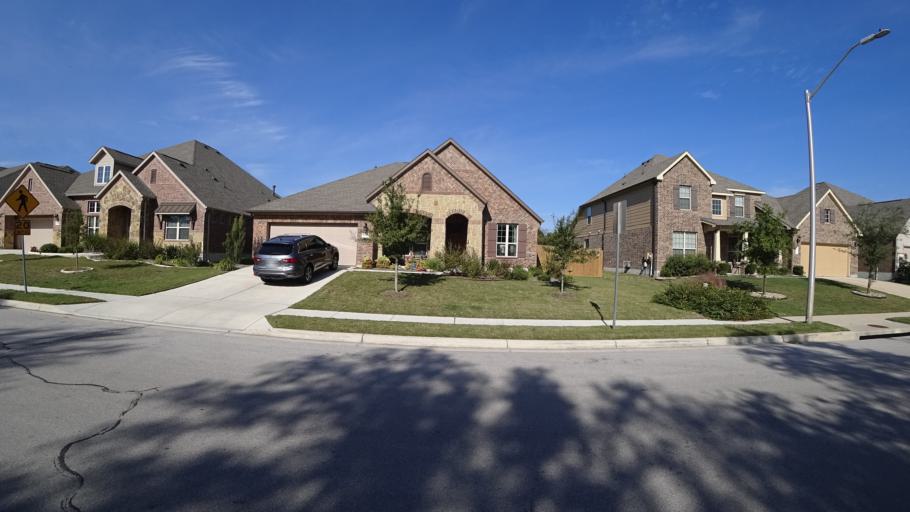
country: US
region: Texas
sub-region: Travis County
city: Barton Creek
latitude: 30.2328
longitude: -97.9074
